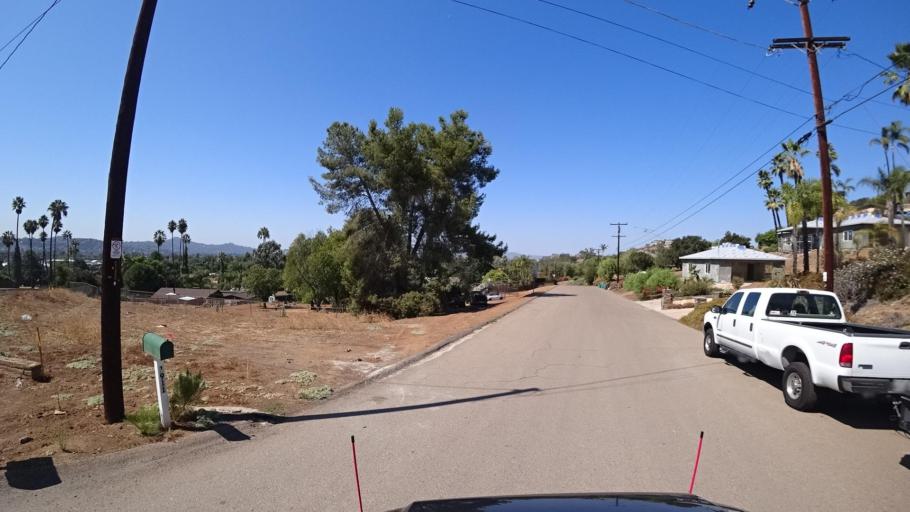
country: US
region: California
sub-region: San Diego County
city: Granite Hills
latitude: 32.8036
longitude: -116.9104
